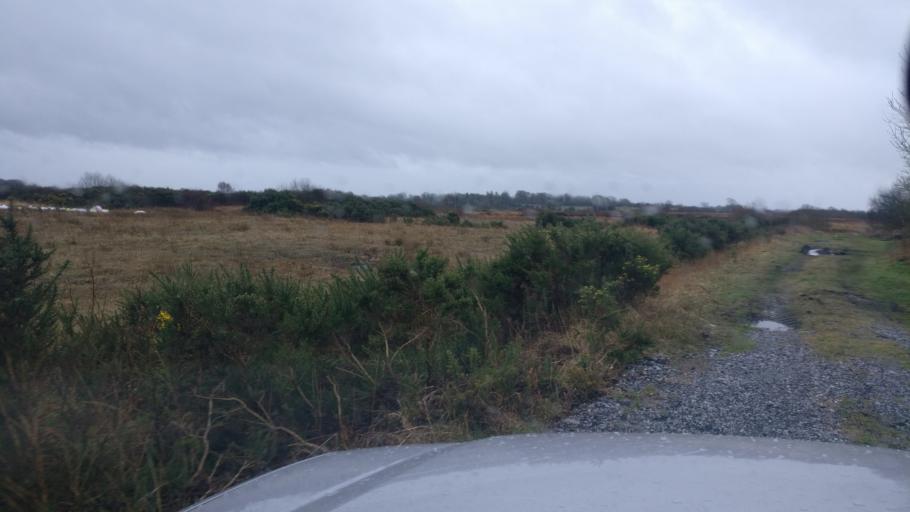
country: IE
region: Connaught
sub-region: County Galway
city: Ballinasloe
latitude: 53.2455
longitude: -8.3267
